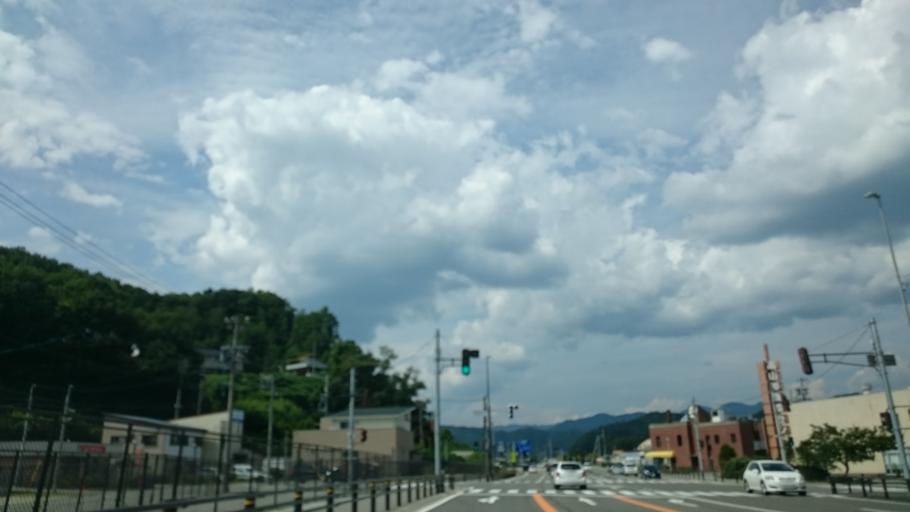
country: JP
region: Gifu
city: Takayama
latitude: 36.1575
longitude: 137.2436
